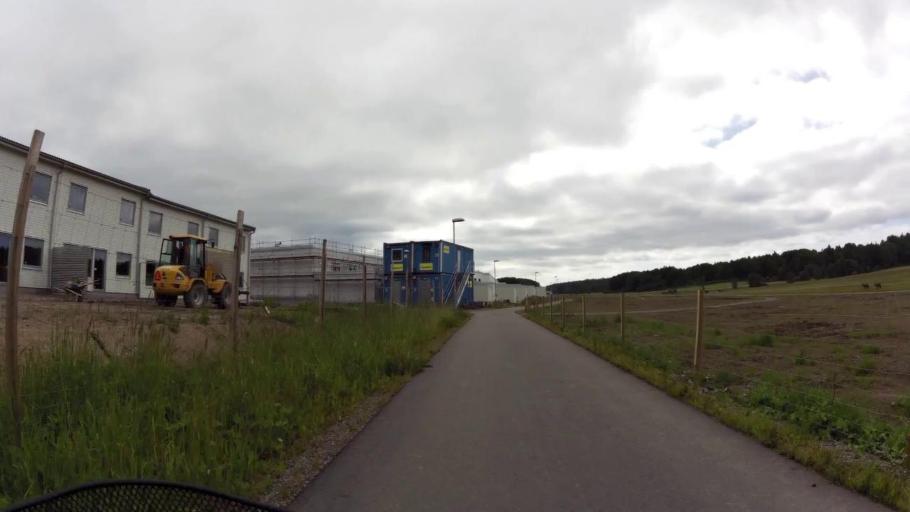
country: SE
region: OEstergoetland
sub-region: Linkopings Kommun
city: Sturefors
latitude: 58.3663
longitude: 15.6743
